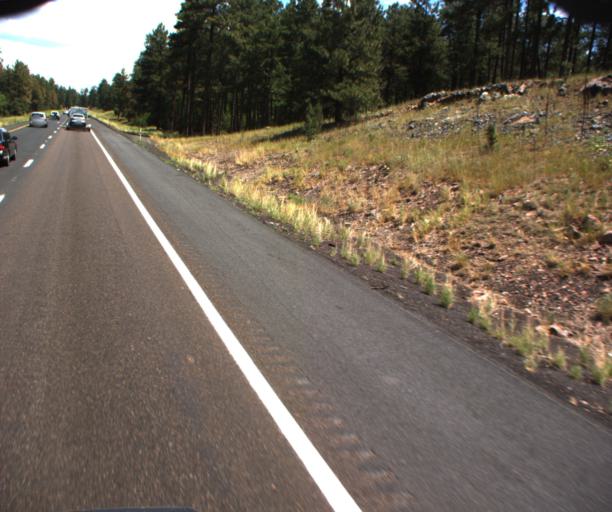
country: US
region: Arizona
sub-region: Coconino County
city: Sedona
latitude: 34.8269
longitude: -111.6084
